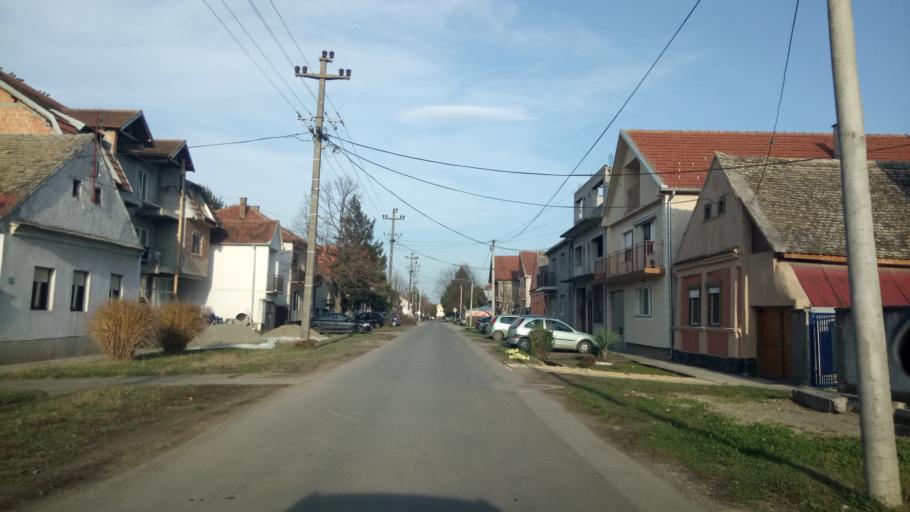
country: RS
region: Autonomna Pokrajina Vojvodina
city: Nova Pazova
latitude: 44.9453
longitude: 20.2301
